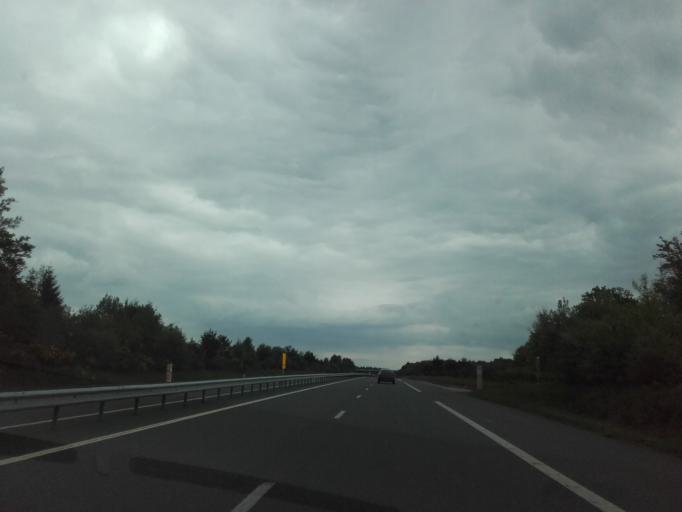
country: FR
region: Limousin
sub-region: Departement de la Correze
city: Ussel
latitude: 45.5979
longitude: 2.4311
